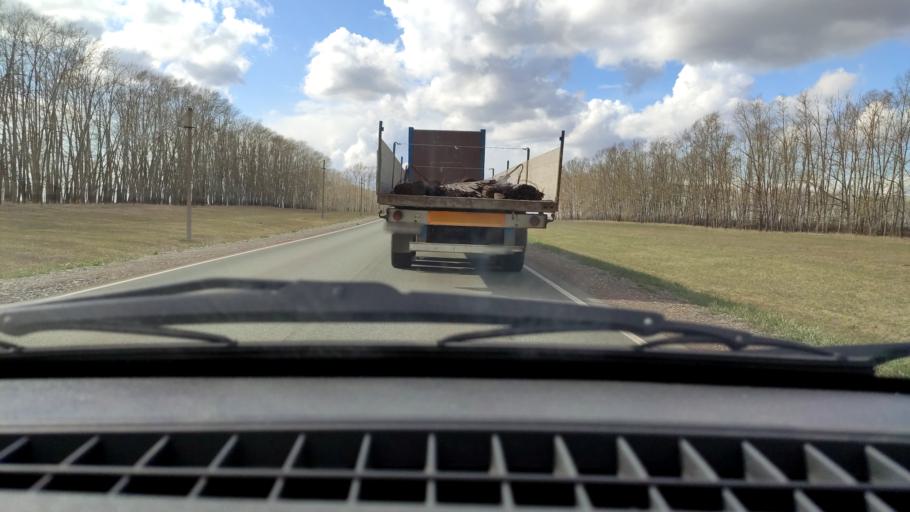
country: RU
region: Bashkortostan
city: Alekseyevka
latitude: 55.0566
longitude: 55.1166
